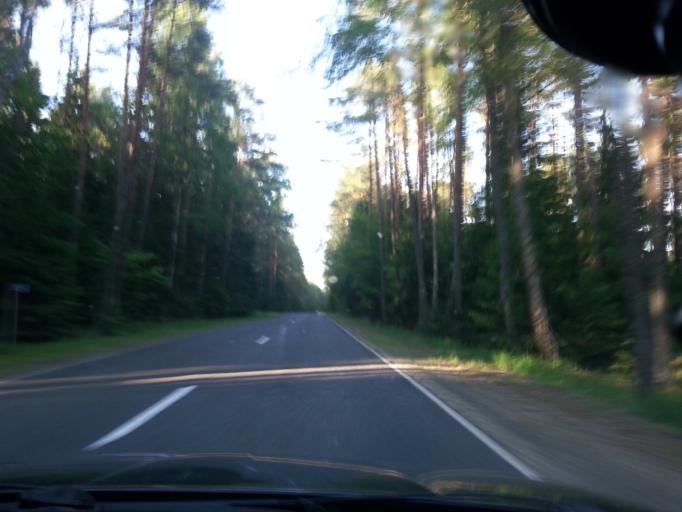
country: BY
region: Minsk
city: Narach
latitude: 54.9437
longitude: 26.5757
